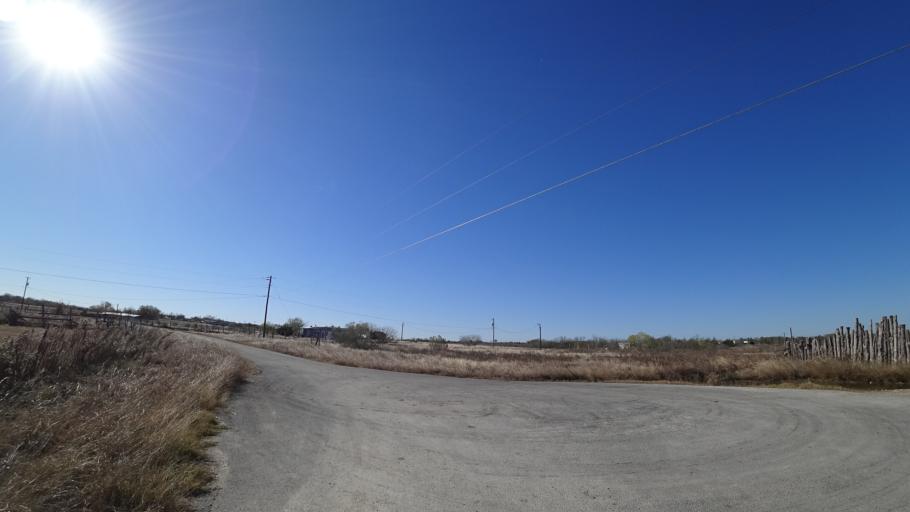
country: US
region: Texas
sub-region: Travis County
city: Onion Creek
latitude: 30.1054
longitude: -97.6848
